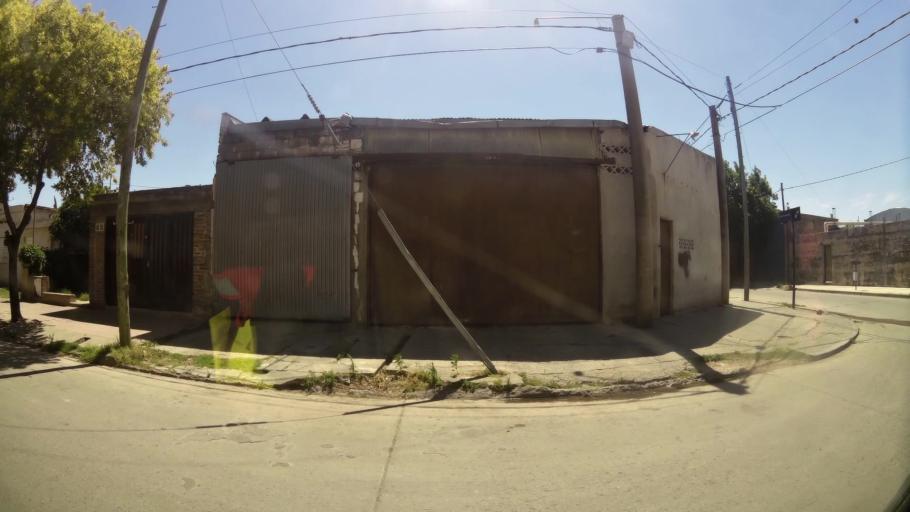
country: AR
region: Cordoba
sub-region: Departamento de Capital
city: Cordoba
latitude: -31.3716
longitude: -64.1491
